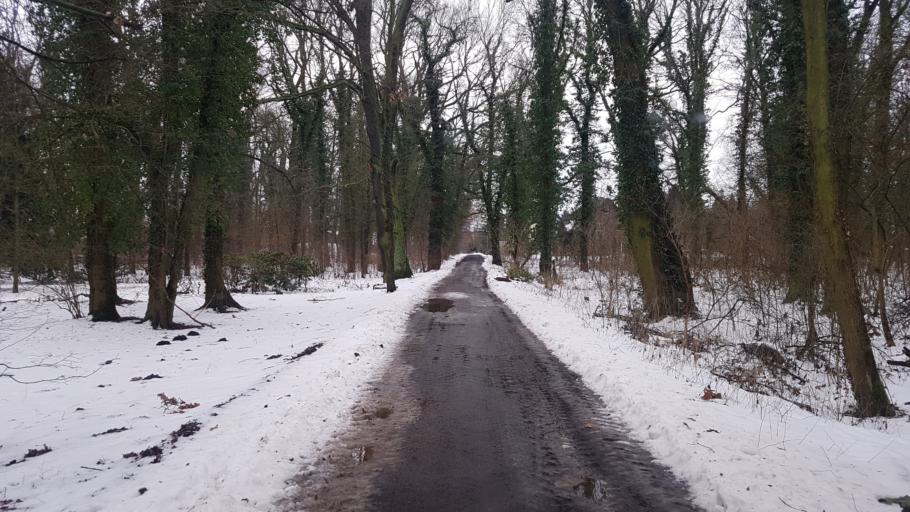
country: DE
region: Brandenburg
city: Bronkow
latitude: 51.6097
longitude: 13.9052
